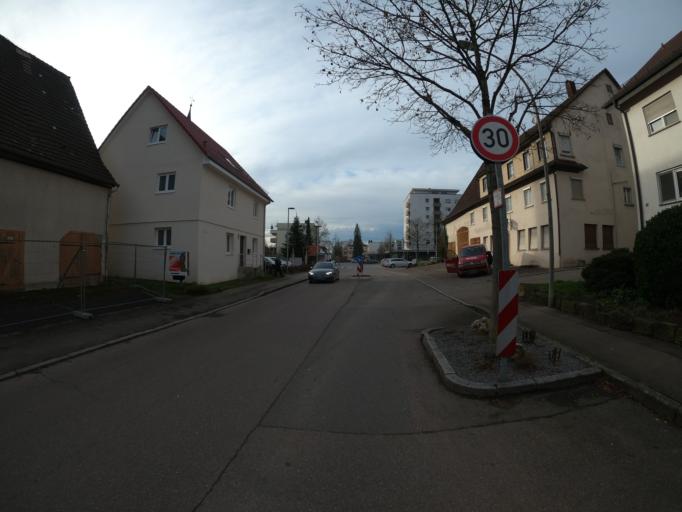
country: DE
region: Baden-Wuerttemberg
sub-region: Regierungsbezirk Stuttgart
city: Rechberghausen
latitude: 48.7244
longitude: 9.6580
